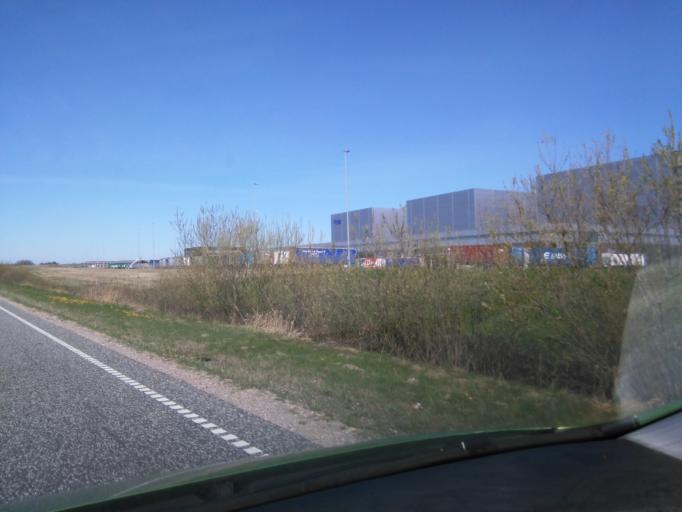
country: DK
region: Central Jutland
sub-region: Hedensted Kommune
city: Hedensted
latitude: 55.8396
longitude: 9.6042
